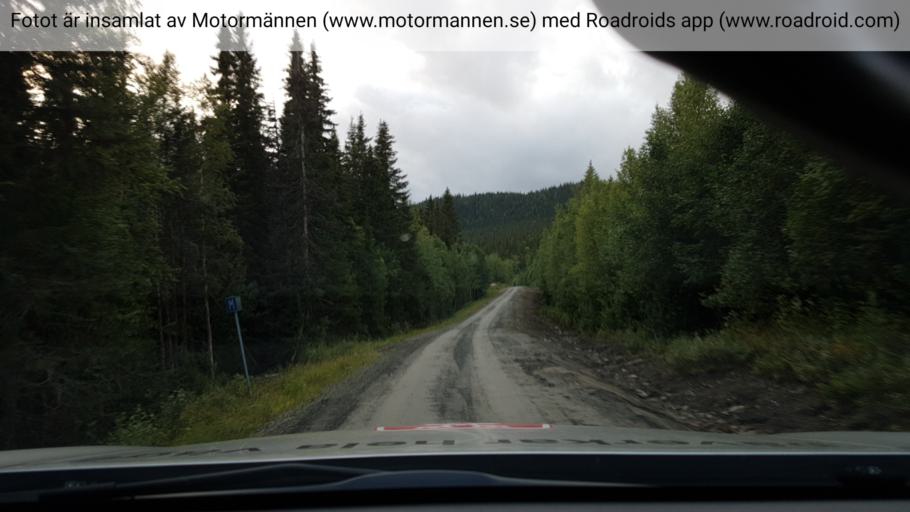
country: SE
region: Vaesterbotten
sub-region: Vilhelmina Kommun
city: Sjoberg
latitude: 65.4982
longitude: 15.5501
